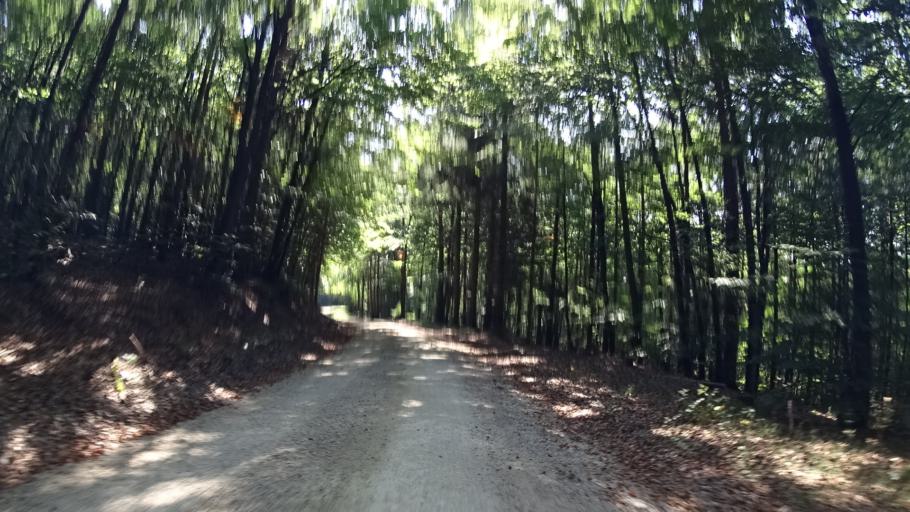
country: DE
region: Bavaria
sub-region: Upper Bavaria
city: Walting
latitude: 48.9731
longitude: 11.3441
